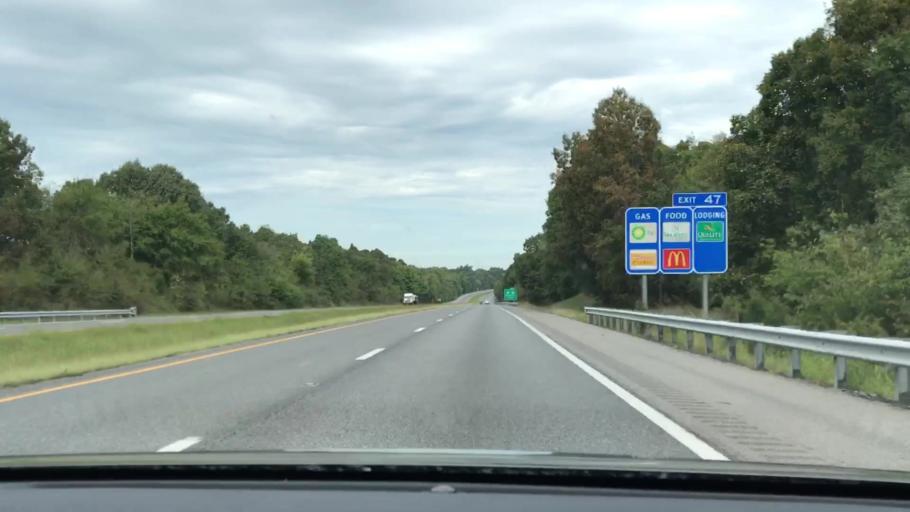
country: US
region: Kentucky
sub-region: Marshall County
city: Benton
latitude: 36.9109
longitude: -88.3493
